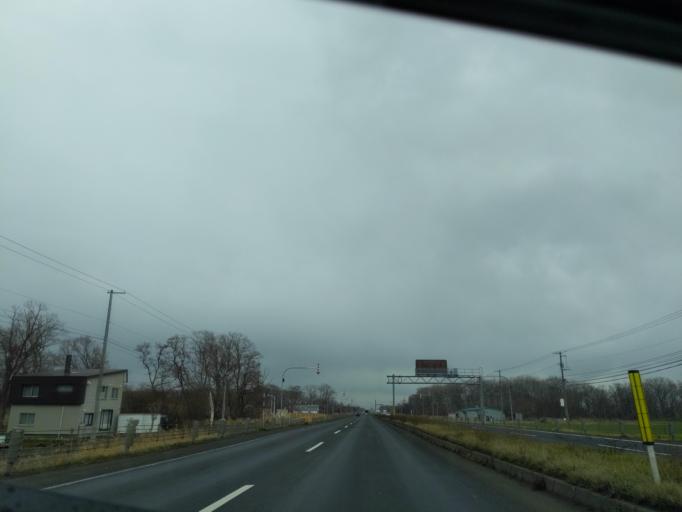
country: JP
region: Hokkaido
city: Ishikari
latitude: 43.1806
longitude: 141.3528
